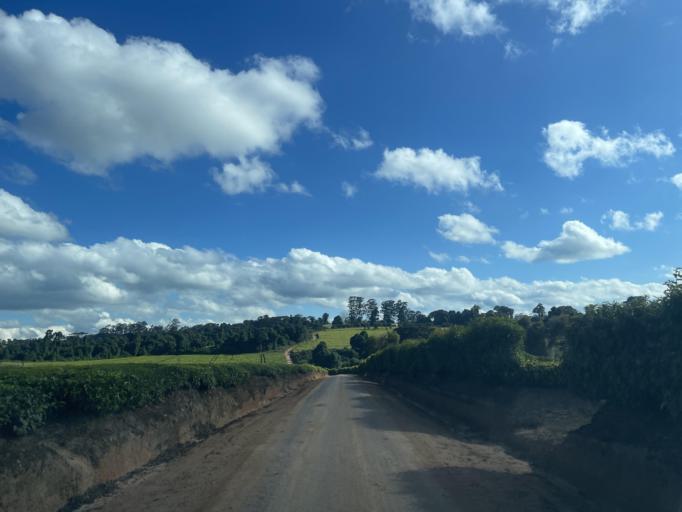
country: TZ
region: Iringa
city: Makungu
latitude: -8.4670
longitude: 35.4269
